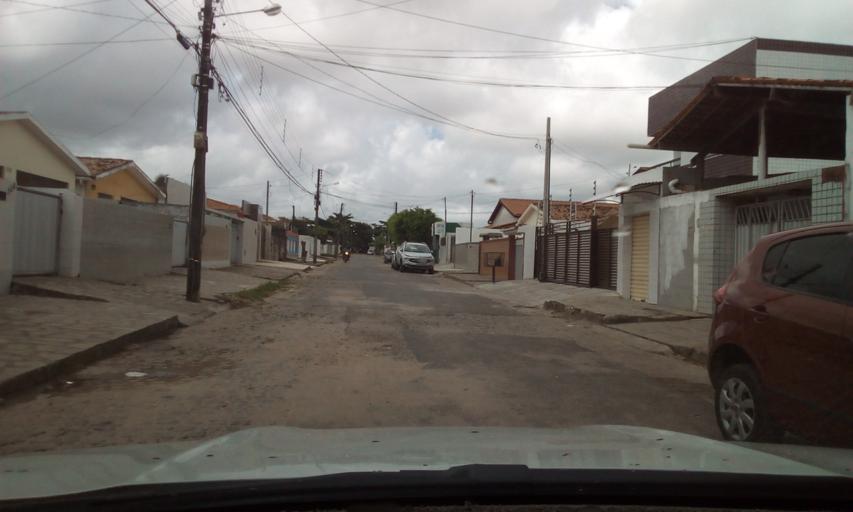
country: BR
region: Paraiba
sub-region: Joao Pessoa
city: Joao Pessoa
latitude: -7.1772
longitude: -34.8646
